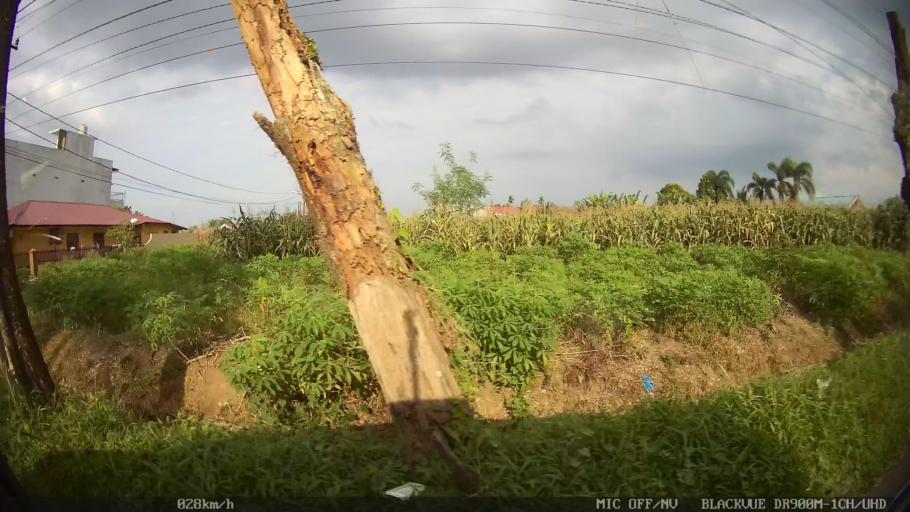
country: ID
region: North Sumatra
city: Sunggal
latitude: 3.5343
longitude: 98.6053
